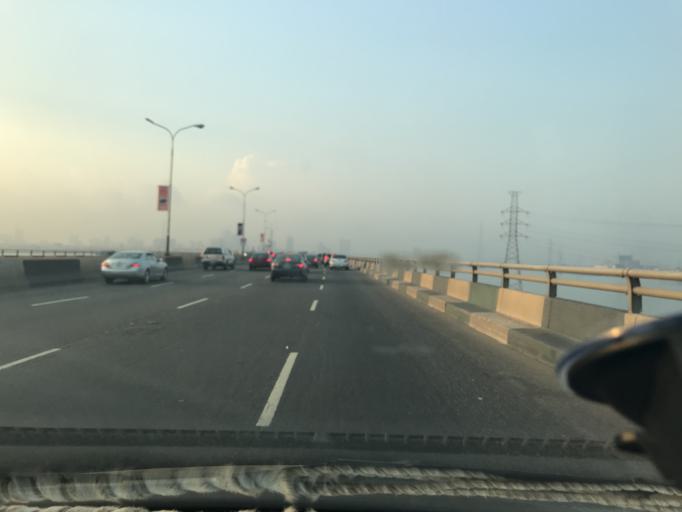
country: NG
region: Lagos
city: Ebute Metta
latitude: 6.4791
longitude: 3.3911
